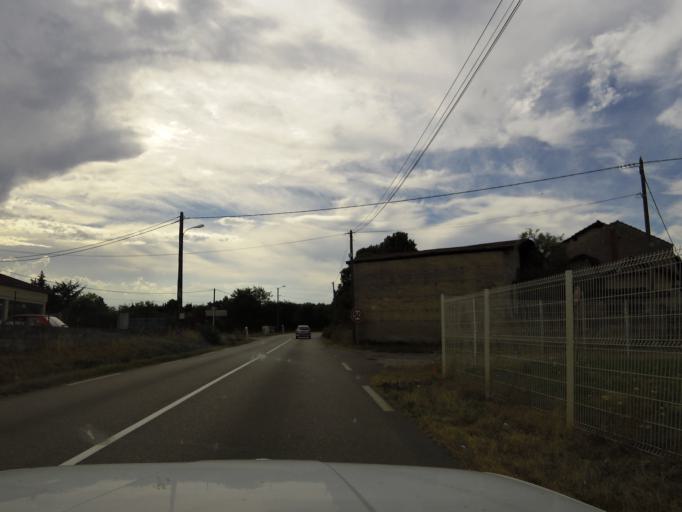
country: FR
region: Rhone-Alpes
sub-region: Departement de l'Ain
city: Meximieux
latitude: 45.8972
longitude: 5.1968
